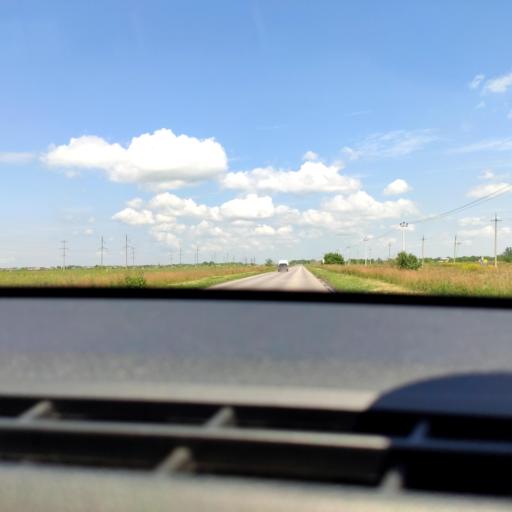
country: RU
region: Samara
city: Podstepki
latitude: 53.5552
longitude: 49.0907
